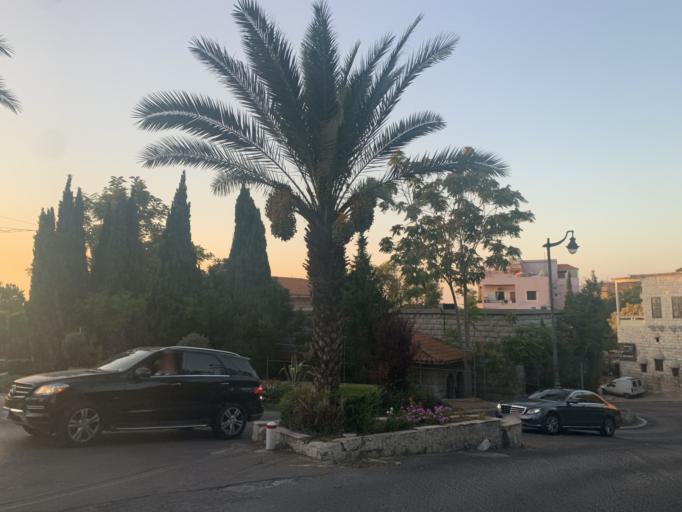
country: LB
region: Mont-Liban
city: Djounie
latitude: 33.9670
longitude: 35.6255
